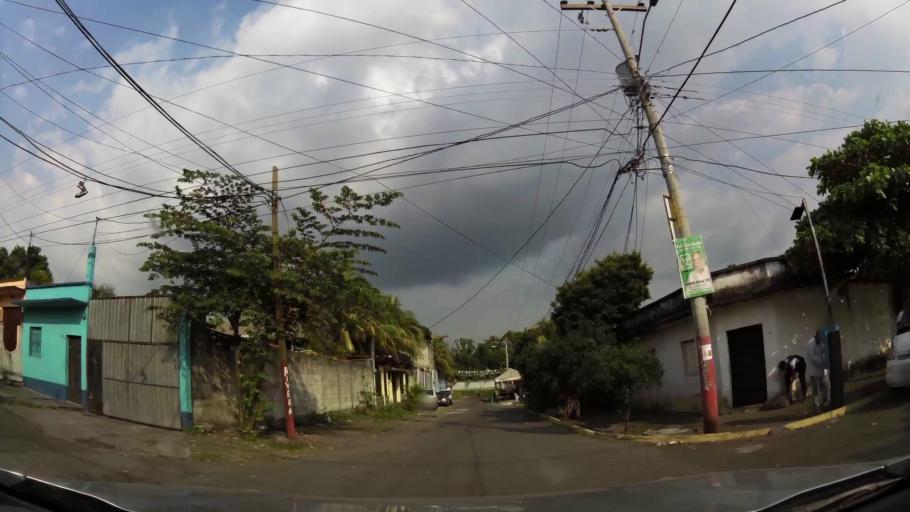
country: GT
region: Escuintla
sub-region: Municipio de Escuintla
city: Escuintla
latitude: 14.3146
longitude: -90.7941
